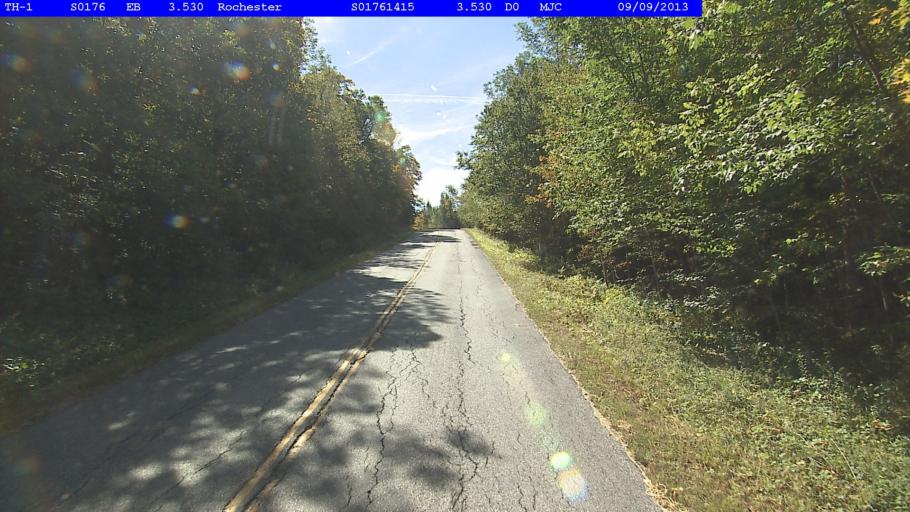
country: US
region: Vermont
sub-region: Orange County
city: Randolph
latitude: 43.8562
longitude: -72.7559
